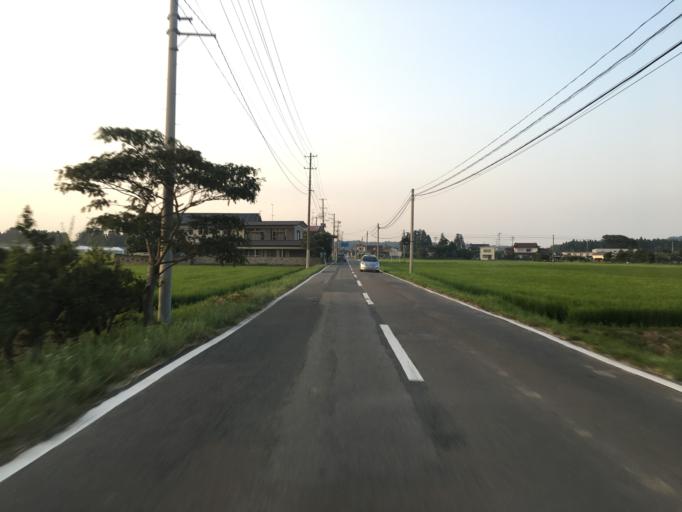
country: JP
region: Fukushima
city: Namie
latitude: 37.7171
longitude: 140.9288
